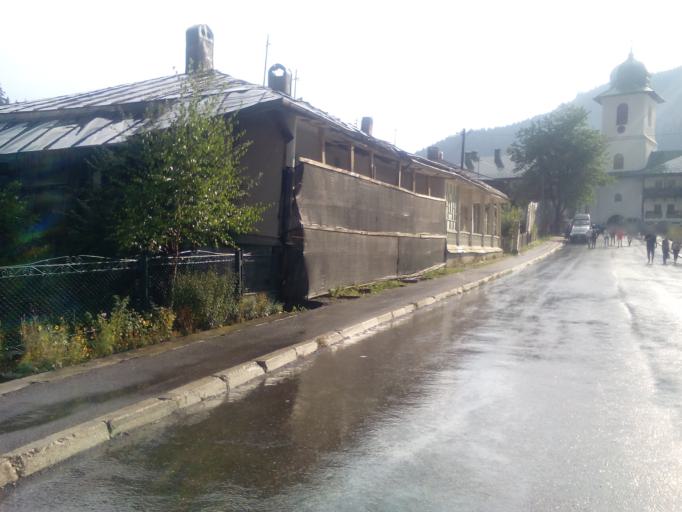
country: RO
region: Neamt
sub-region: Comuna Agapia
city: Filioara
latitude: 47.1709
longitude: 26.2372
